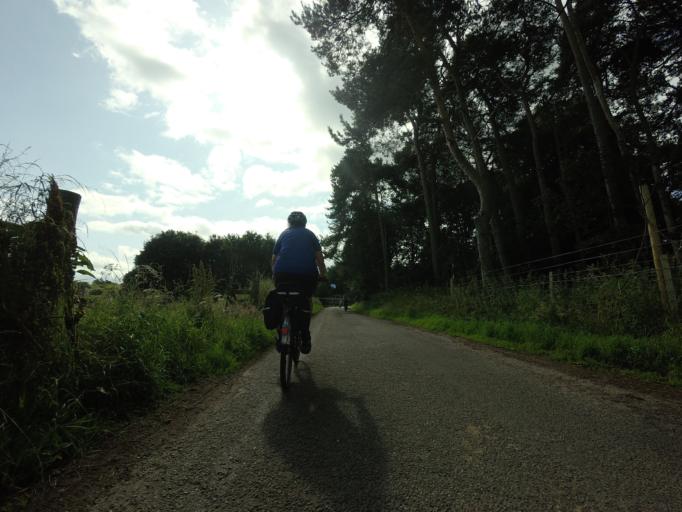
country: GB
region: Scotland
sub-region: Highland
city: Nairn
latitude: 57.5687
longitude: -3.8668
